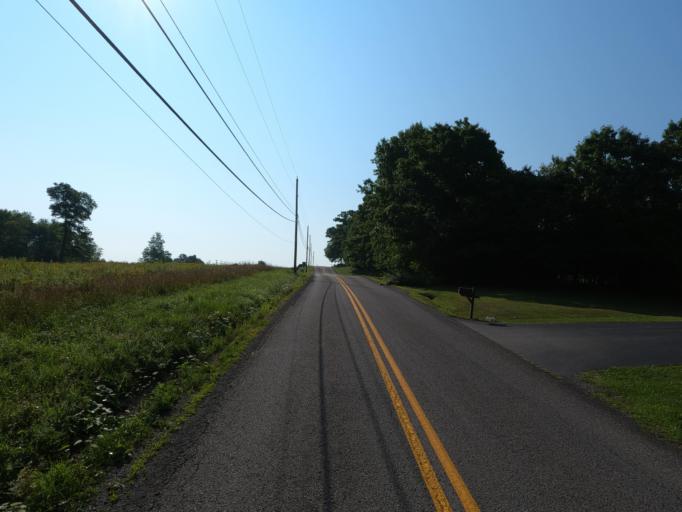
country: US
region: Maryland
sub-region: Garrett County
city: Oakland
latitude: 39.4987
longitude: -79.3986
